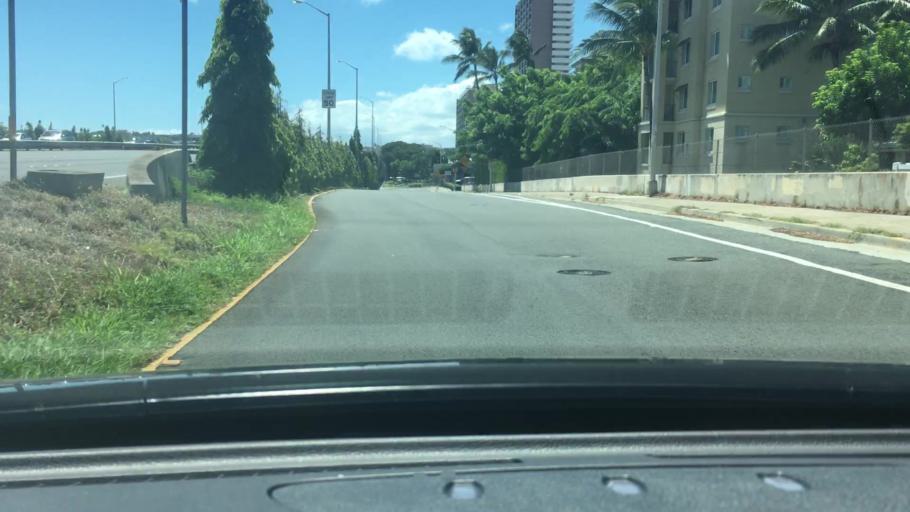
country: US
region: Hawaii
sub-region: Honolulu County
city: Honolulu
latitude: 21.2783
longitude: -157.7817
